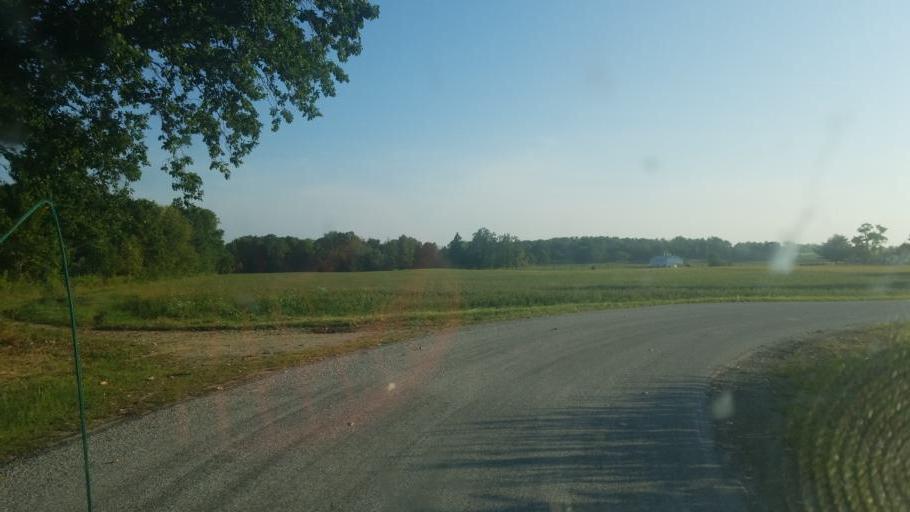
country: US
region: Ohio
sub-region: Huron County
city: Greenwich
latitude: 40.9096
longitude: -82.4683
